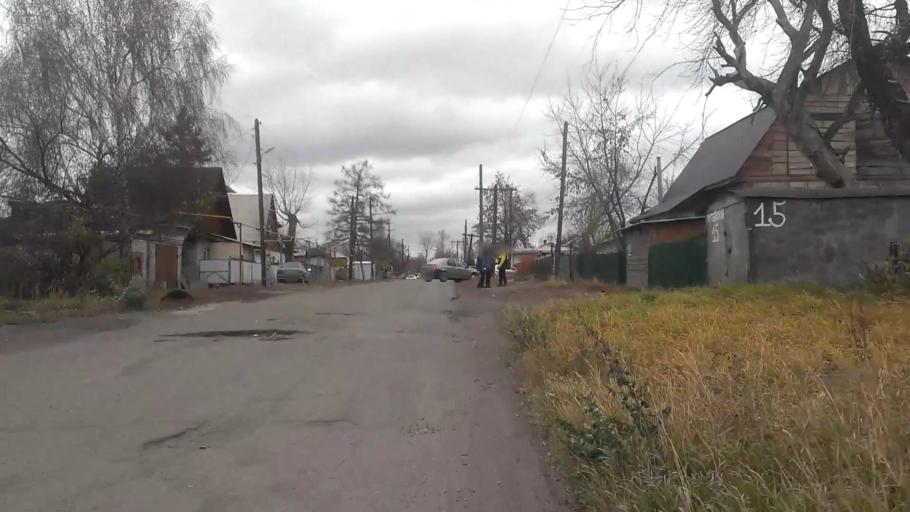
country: RU
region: Altai Krai
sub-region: Gorod Barnaulskiy
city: Barnaul
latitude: 53.3517
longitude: 83.7524
